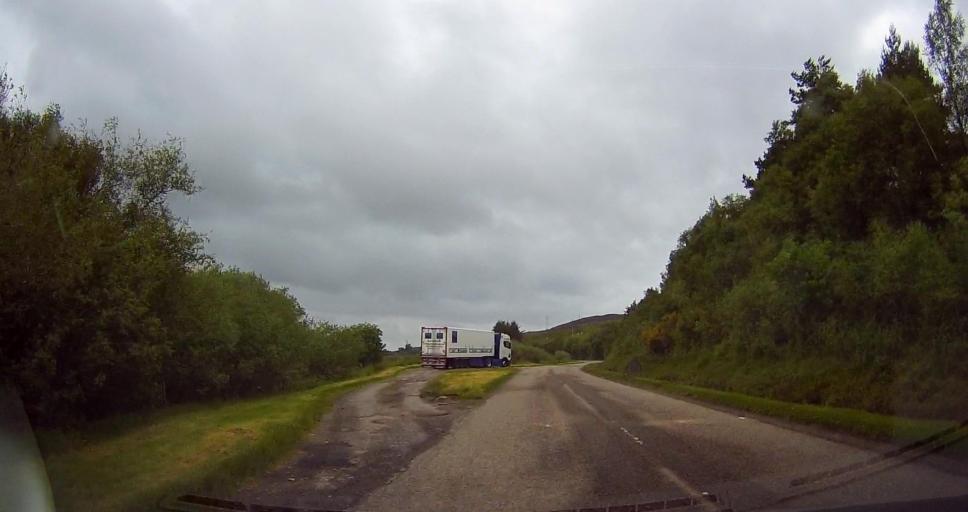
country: GB
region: Scotland
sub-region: Highland
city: Alness
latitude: 58.0180
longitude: -4.3301
